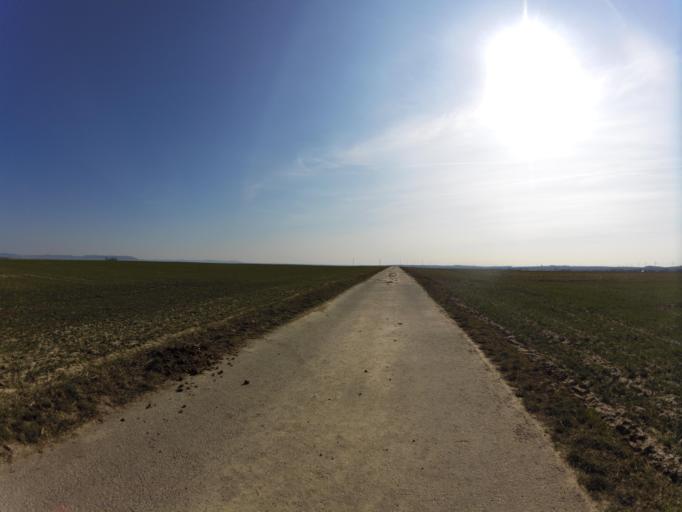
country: DE
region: Bavaria
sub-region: Regierungsbezirk Unterfranken
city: Prosselsheim
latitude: 49.8347
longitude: 10.1210
